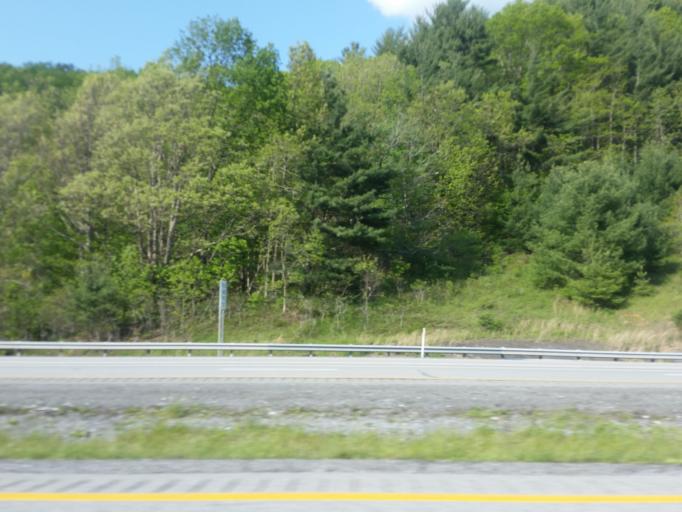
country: US
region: West Virginia
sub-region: Mercer County
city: Athens
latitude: 37.4987
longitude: -81.1079
